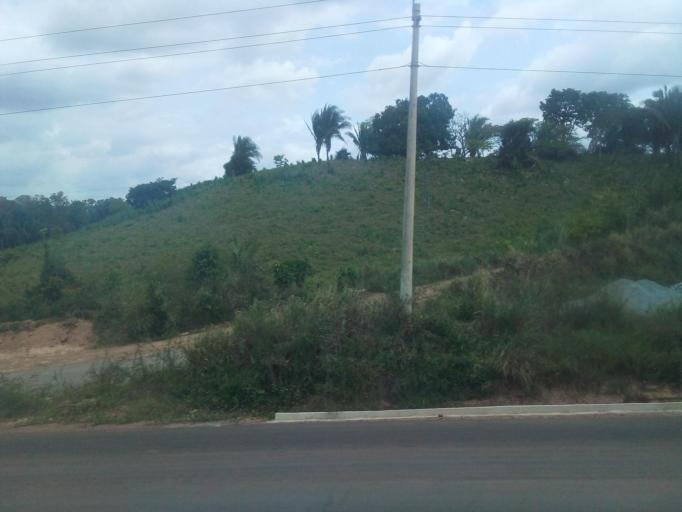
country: BR
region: Maranhao
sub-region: Santa Ines
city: Santa Ines
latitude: -3.7081
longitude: -46.0232
